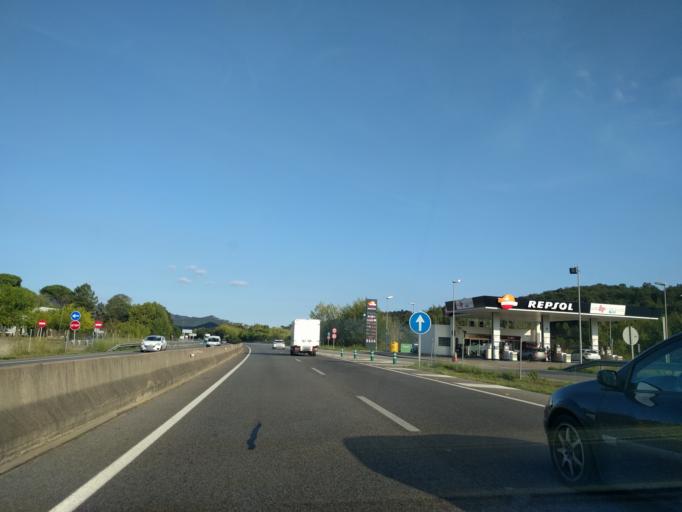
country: ES
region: Catalonia
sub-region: Provincia de Girona
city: Llagostera
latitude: 41.8270
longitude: 2.9471
